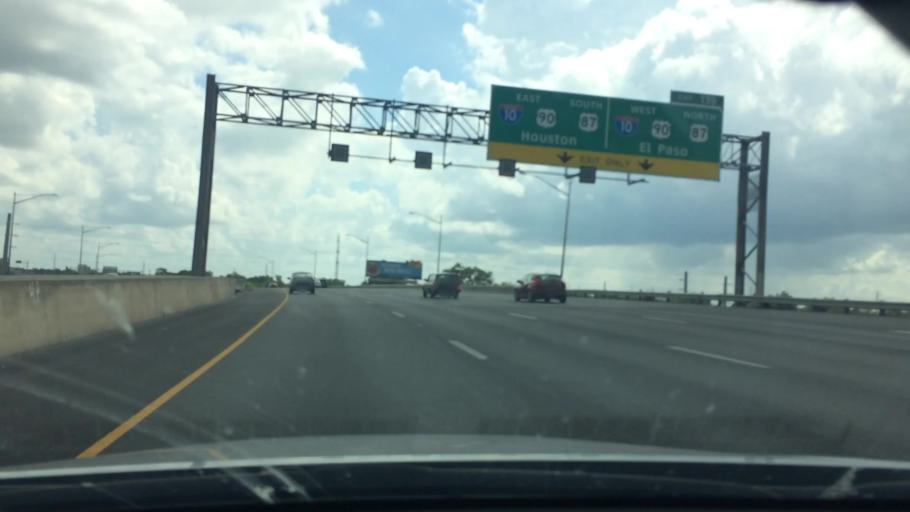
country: US
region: Texas
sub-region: Bexar County
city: San Antonio
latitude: 29.4036
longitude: -98.4810
